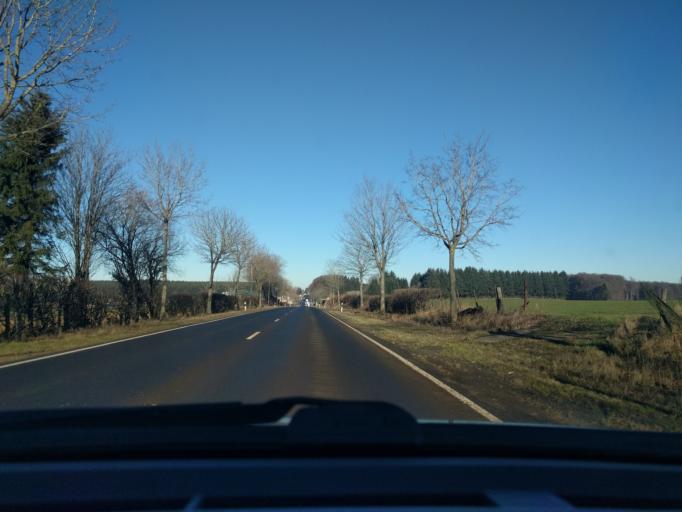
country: LU
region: Diekirch
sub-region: Canton de Clervaux
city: Troisvierges
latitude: 50.1664
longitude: 6.0258
